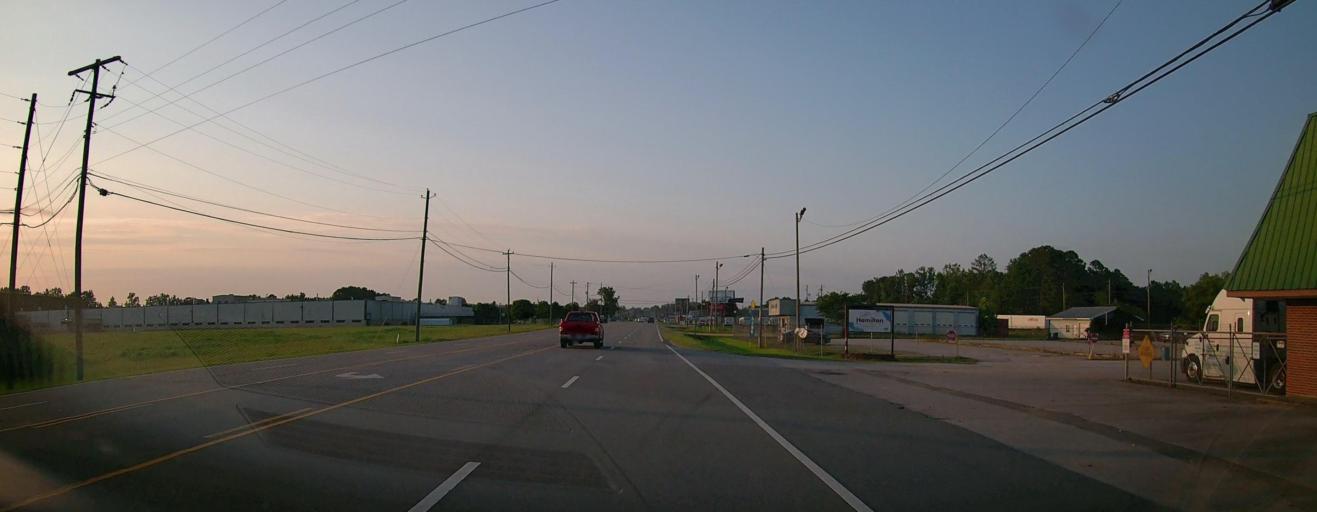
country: US
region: Alabama
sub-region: Marion County
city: Hamilton
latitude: 34.1110
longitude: -87.9893
